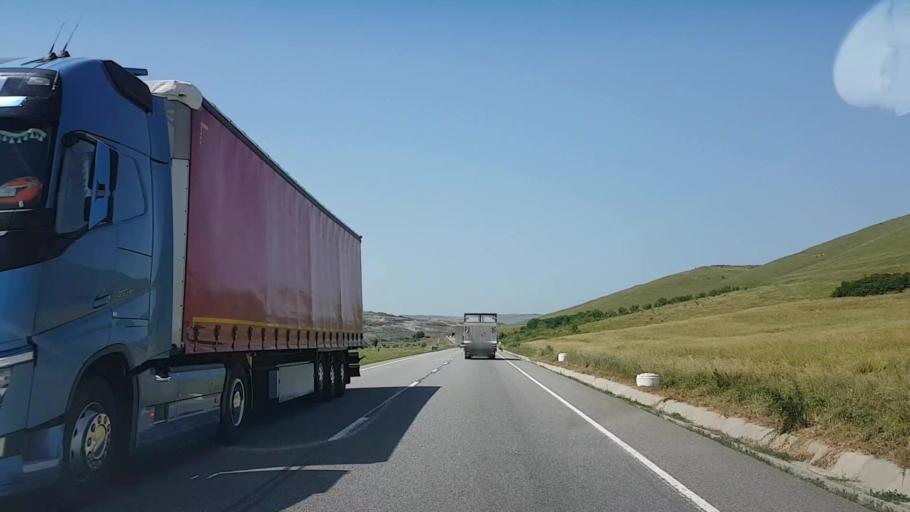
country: RO
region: Cluj
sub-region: Comuna Apahida
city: Dezmir
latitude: 46.7546
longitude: 23.7008
